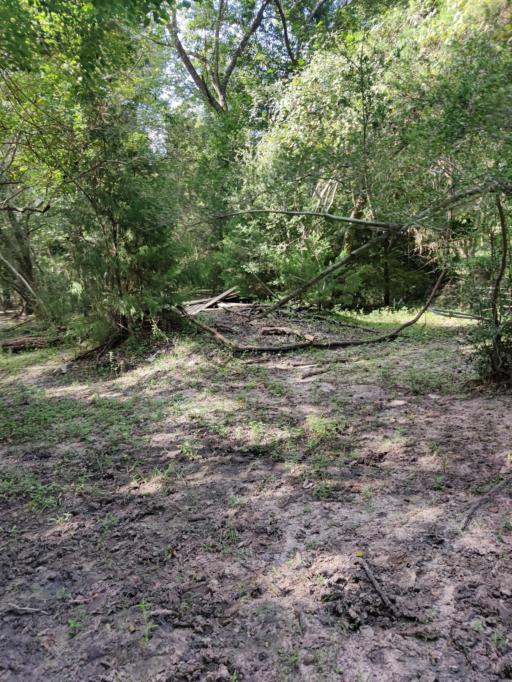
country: US
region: Texas
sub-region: Harris County
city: Oak Cliff Place
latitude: 29.8317
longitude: -95.6644
